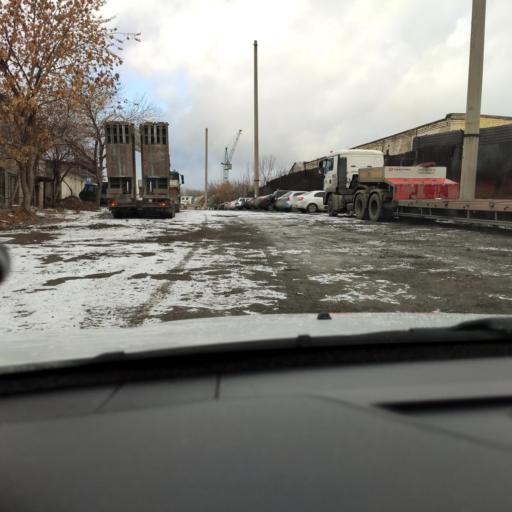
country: RU
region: Samara
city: Samara
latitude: 53.1809
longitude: 50.1531
